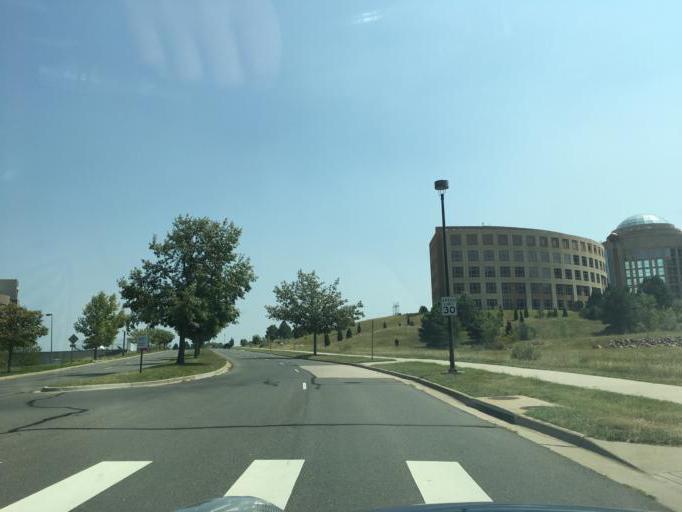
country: US
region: Colorado
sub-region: Jefferson County
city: West Pleasant View
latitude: 39.7298
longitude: -105.2039
